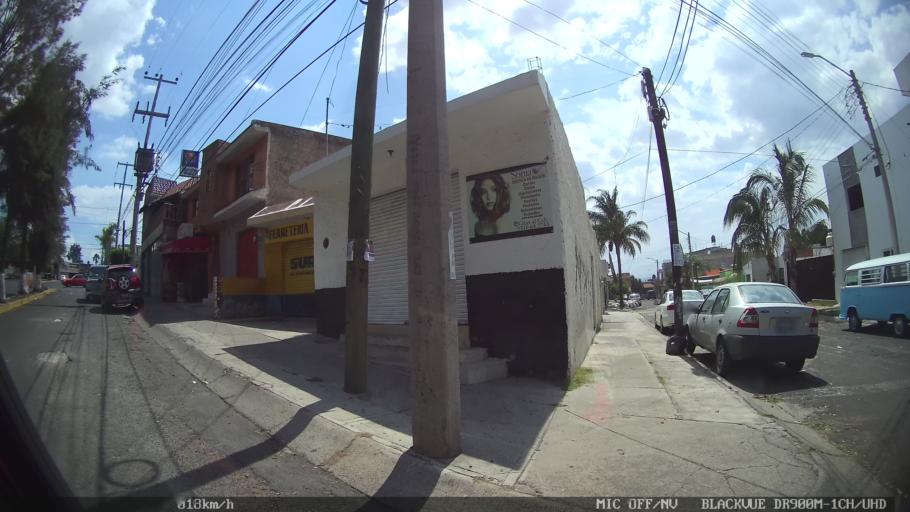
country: MX
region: Jalisco
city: Tonala
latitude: 20.6222
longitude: -103.2586
